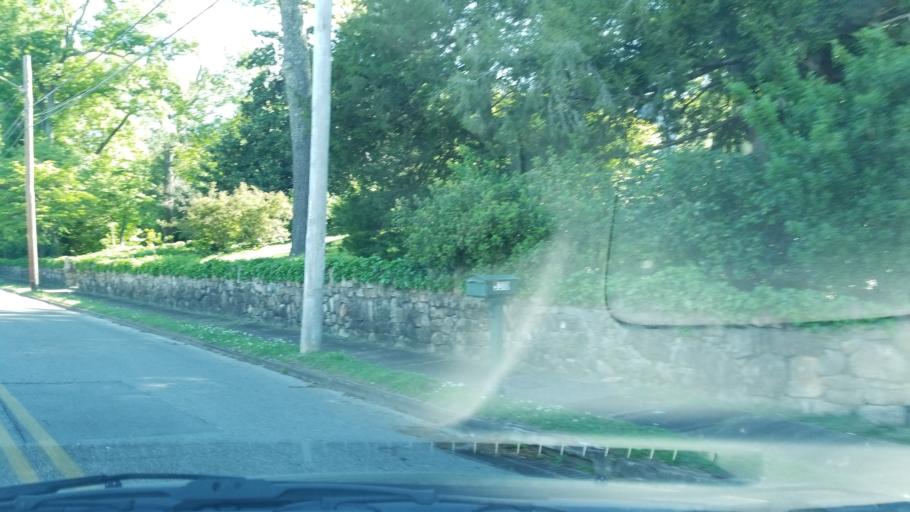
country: US
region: Tennessee
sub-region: Hamilton County
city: Lookout Mountain
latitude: 34.9896
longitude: -85.3277
